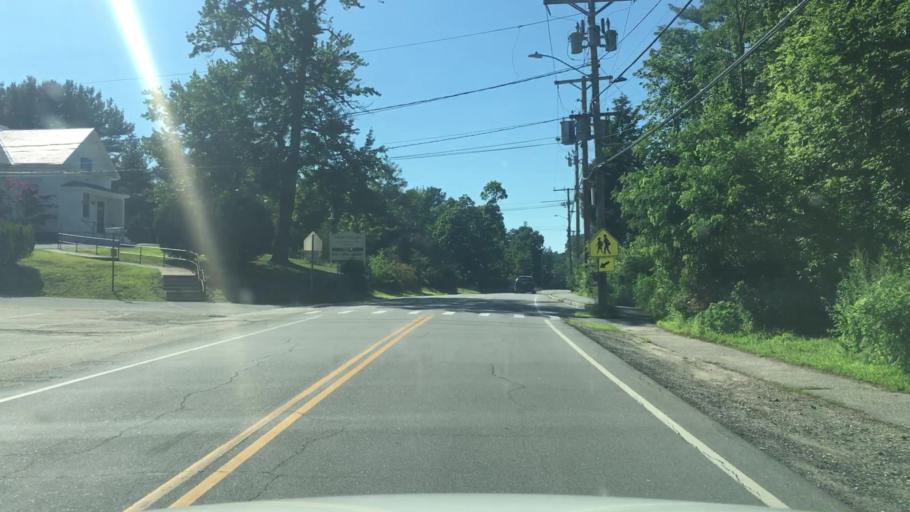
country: US
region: New Hampshire
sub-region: Rockingham County
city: Newmarket
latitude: 43.0352
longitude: -70.9438
